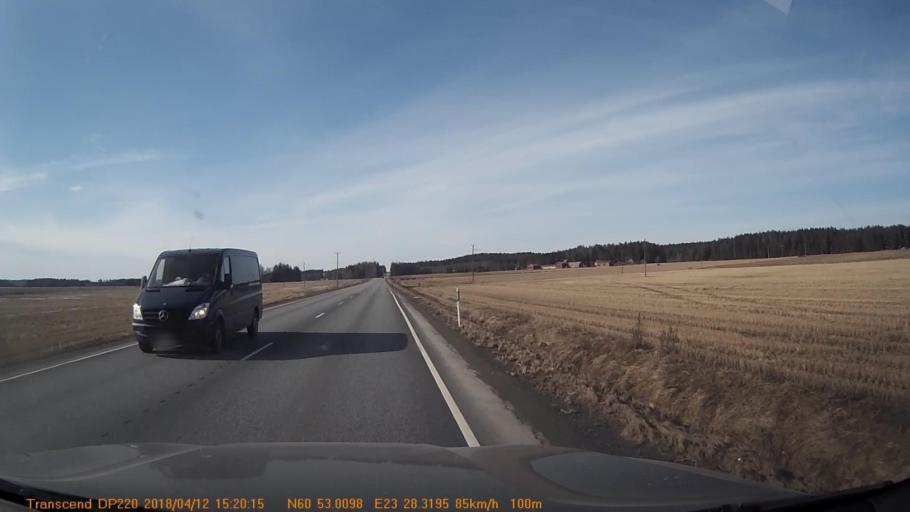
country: FI
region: Haeme
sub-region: Forssa
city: Jokioinen
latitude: 60.8837
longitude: 23.4715
